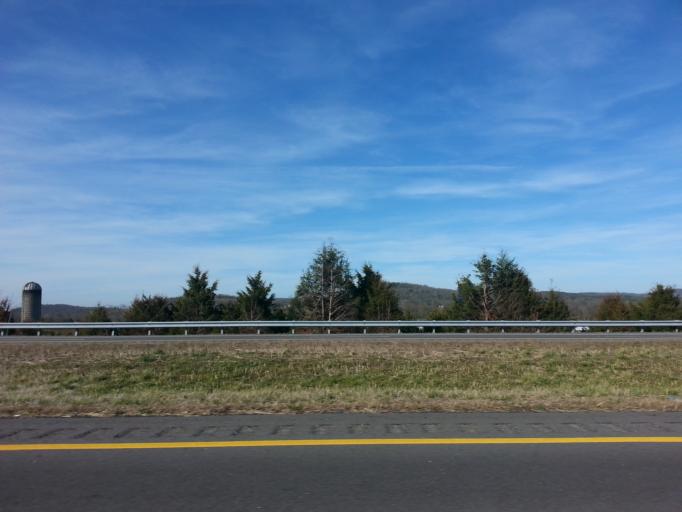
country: US
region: Tennessee
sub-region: Cannon County
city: Woodbury
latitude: 35.8070
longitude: -86.1634
